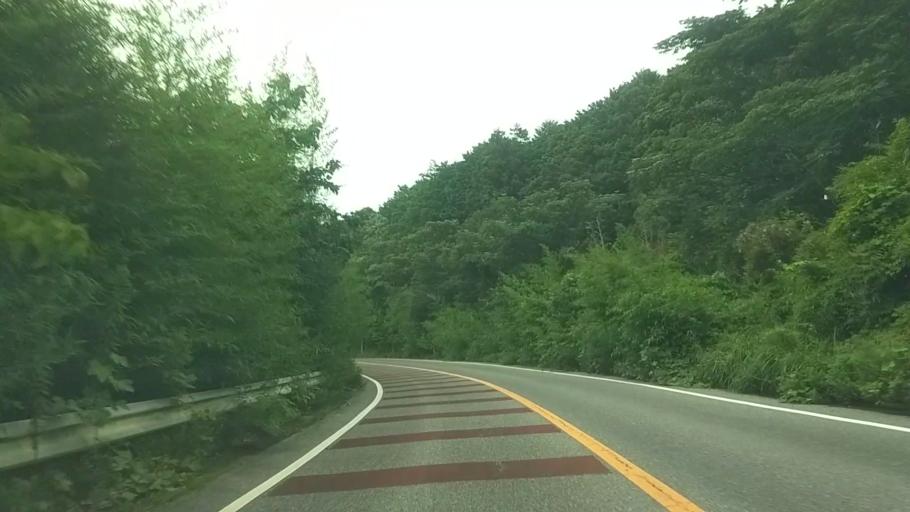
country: JP
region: Chiba
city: Kimitsu
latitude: 35.2380
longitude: 140.0069
